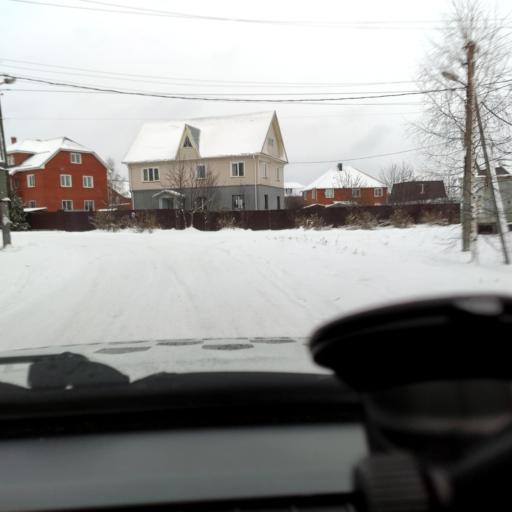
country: RU
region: Perm
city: Perm
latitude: 58.0504
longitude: 56.3555
